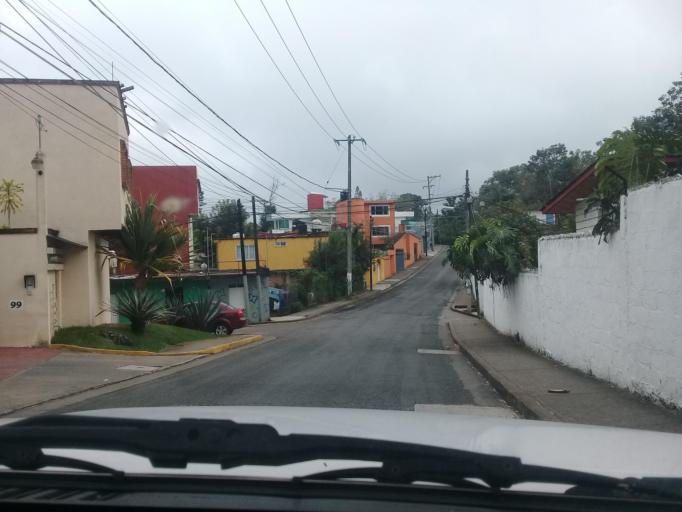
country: MX
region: Veracruz
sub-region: Xalapa
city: Xalapa de Enriquez
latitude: 19.5134
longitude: -96.9105
